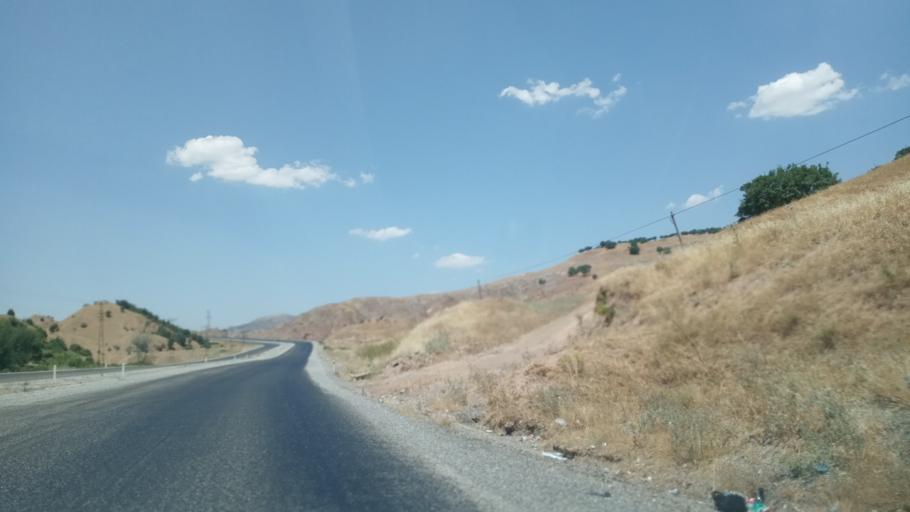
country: TR
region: Batman
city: Kozluk
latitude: 38.1704
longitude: 41.4535
